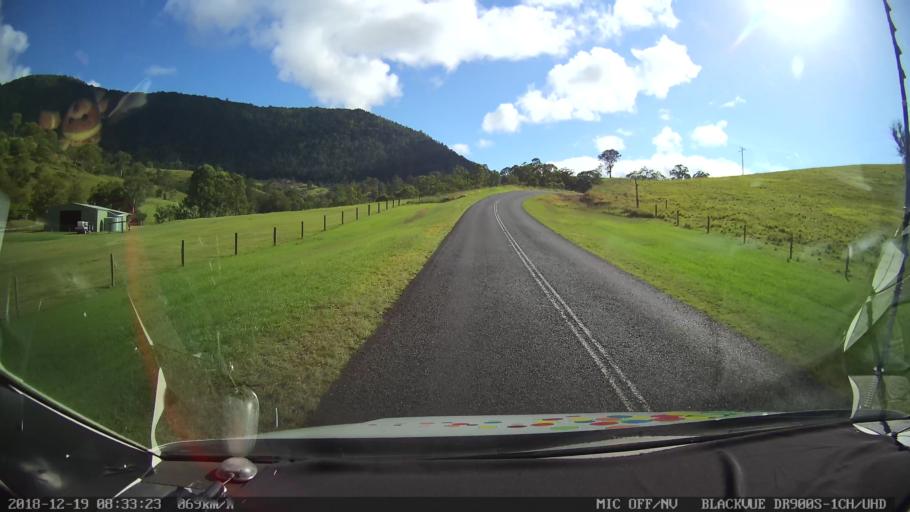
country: AU
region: New South Wales
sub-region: Kyogle
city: Kyogle
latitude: -28.3208
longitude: 152.9496
